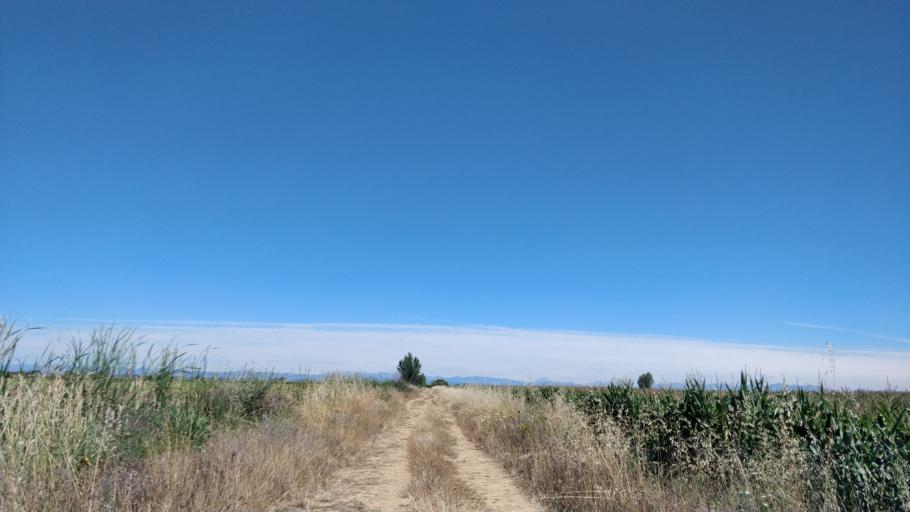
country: ES
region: Castille and Leon
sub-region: Provincia de Leon
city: Bustillo del Paramo
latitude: 42.4477
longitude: -5.8156
